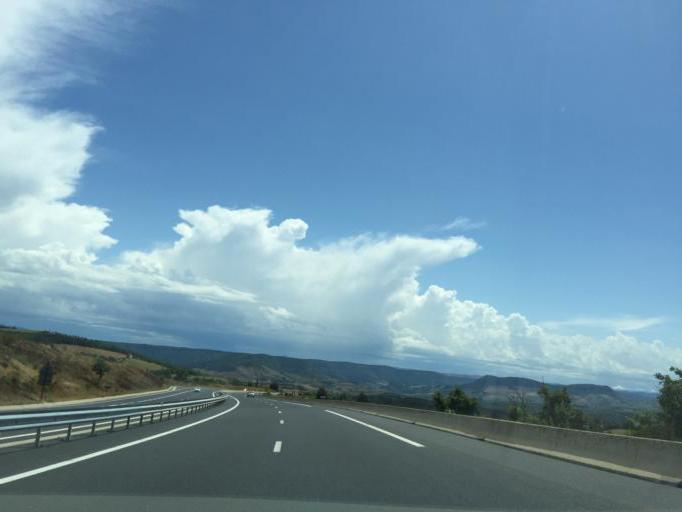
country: FR
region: Midi-Pyrenees
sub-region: Departement de l'Aveyron
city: Severac-le-Chateau
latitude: 44.2426
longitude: 3.0555
